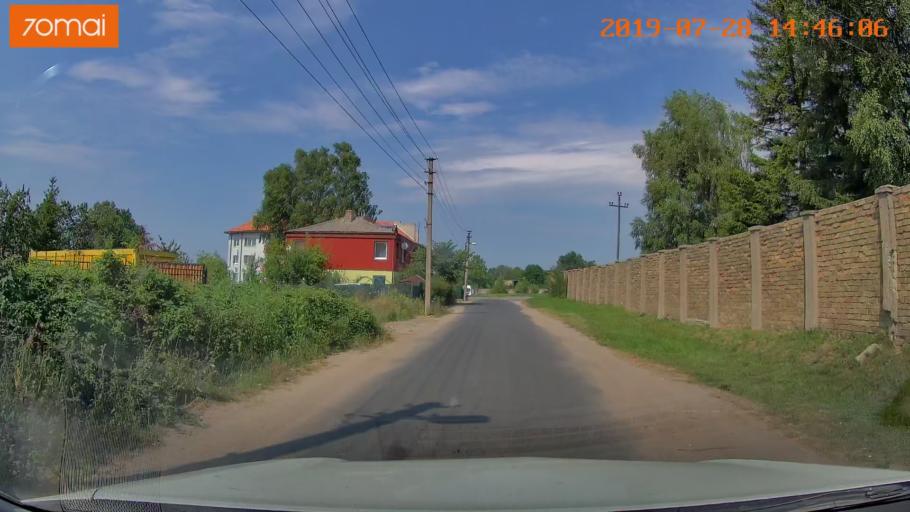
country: RU
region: Kaliningrad
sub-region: Gorod Kaliningrad
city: Yantarnyy
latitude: 54.8747
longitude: 19.9395
